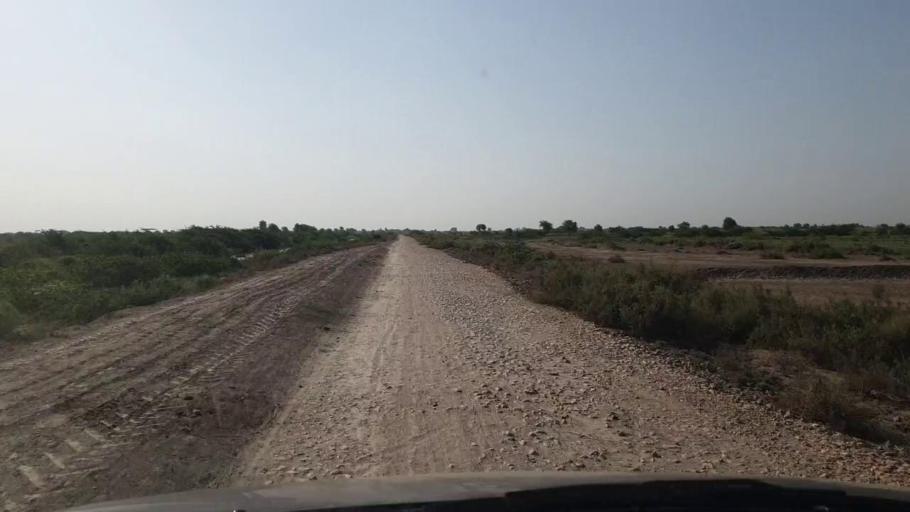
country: PK
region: Sindh
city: Kadhan
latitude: 24.6304
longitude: 69.0729
